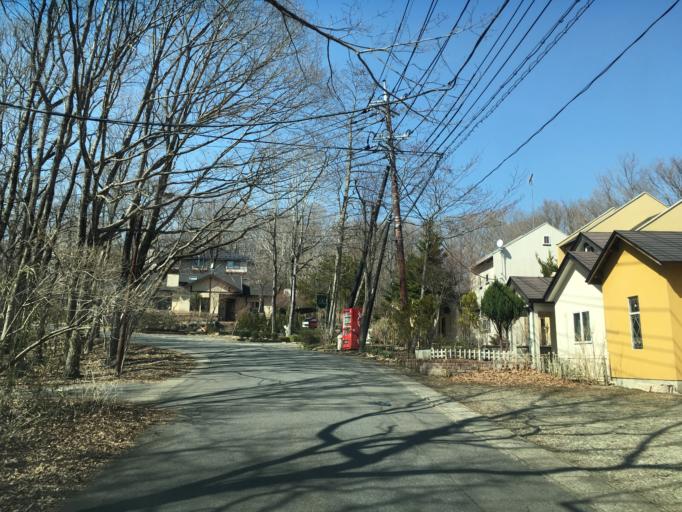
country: JP
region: Tochigi
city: Kuroiso
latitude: 37.0755
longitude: 140.0041
